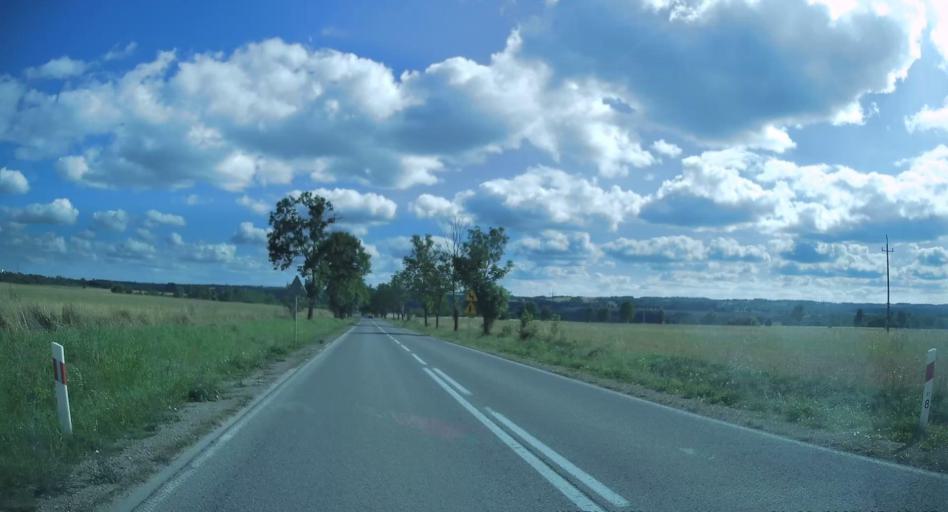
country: PL
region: Swietokrzyskie
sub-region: Powiat kielecki
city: Lagow
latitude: 50.7900
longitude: 21.0817
